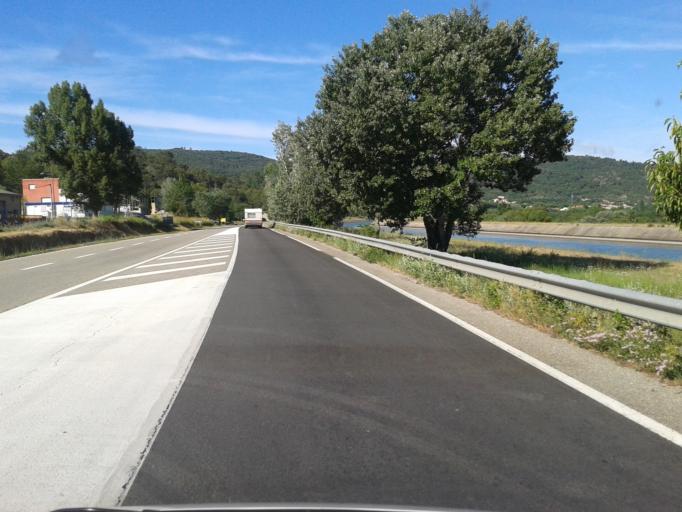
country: FR
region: Provence-Alpes-Cote d'Azur
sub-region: Departement du Vaucluse
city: Beaumont-de-Pertuis
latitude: 43.6915
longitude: 5.7243
